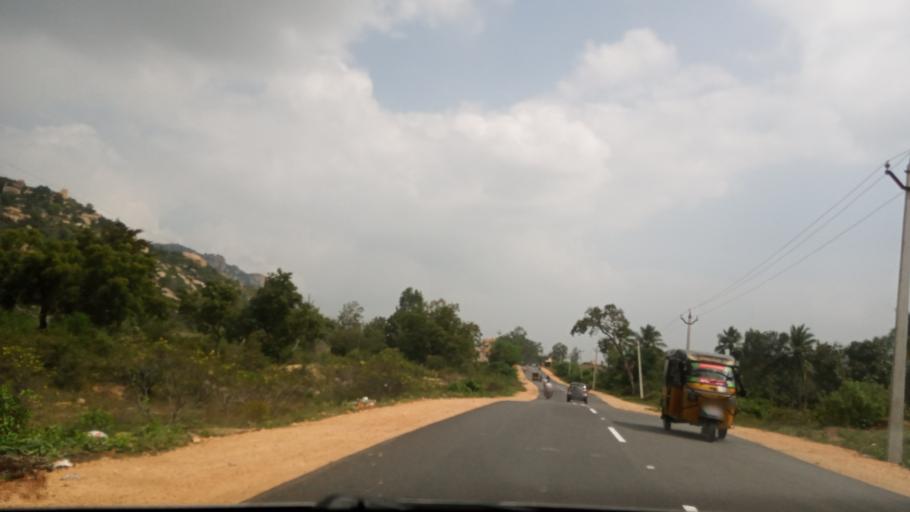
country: IN
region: Andhra Pradesh
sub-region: Chittoor
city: Madanapalle
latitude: 13.6367
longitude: 78.5943
